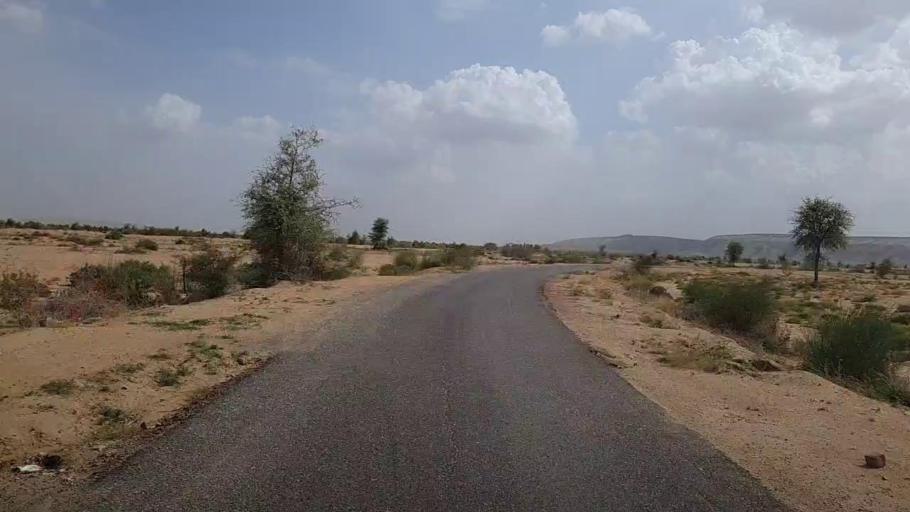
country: PK
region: Sindh
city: Jamshoro
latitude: 25.3983
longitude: 67.7659
